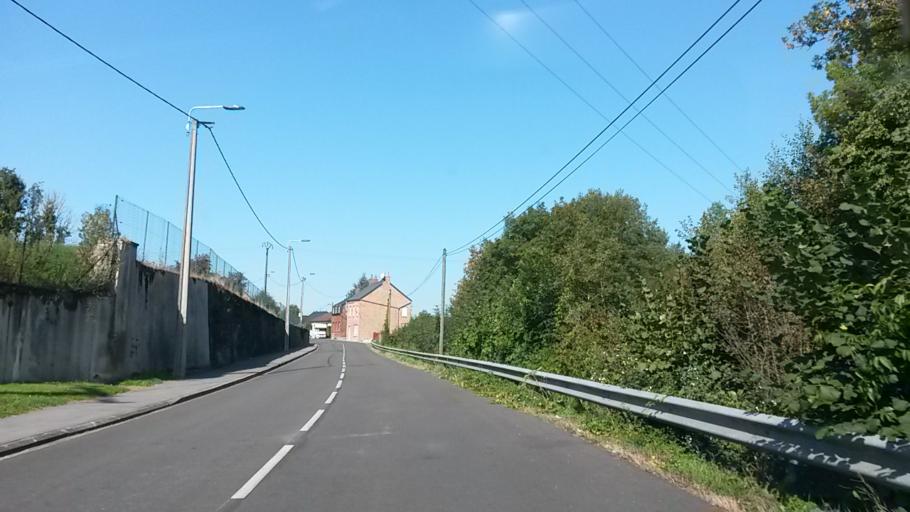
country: FR
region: Nord-Pas-de-Calais
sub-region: Departement du Nord
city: Avesnelles
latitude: 50.1217
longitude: 3.9483
